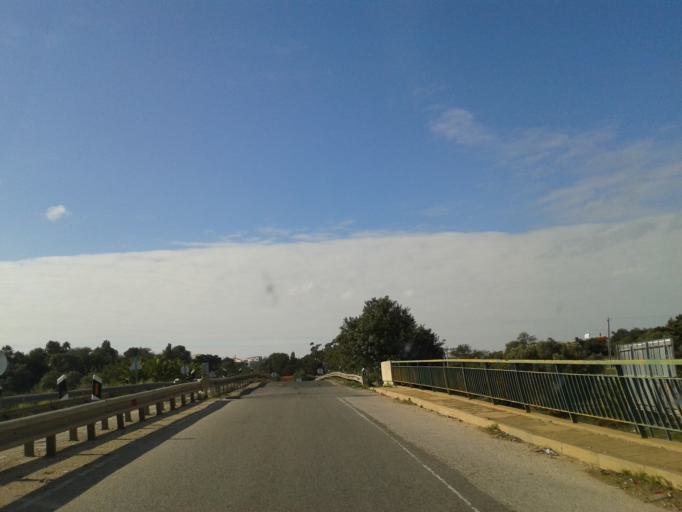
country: PT
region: Faro
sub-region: Loule
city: Almancil
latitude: 37.0840
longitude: -8.0135
